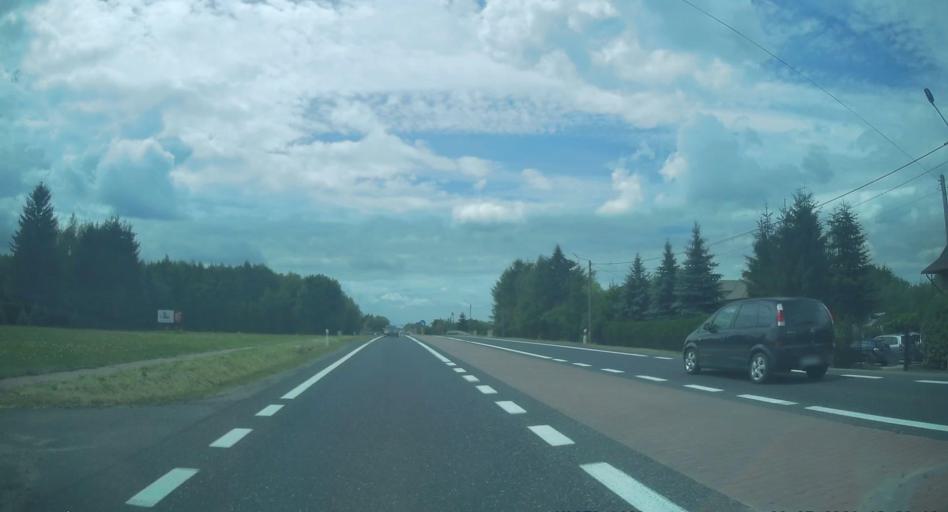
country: PL
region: Subcarpathian Voivodeship
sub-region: Powiat ropczycko-sedziszowski
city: Ostrow
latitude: 50.0621
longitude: 21.5370
